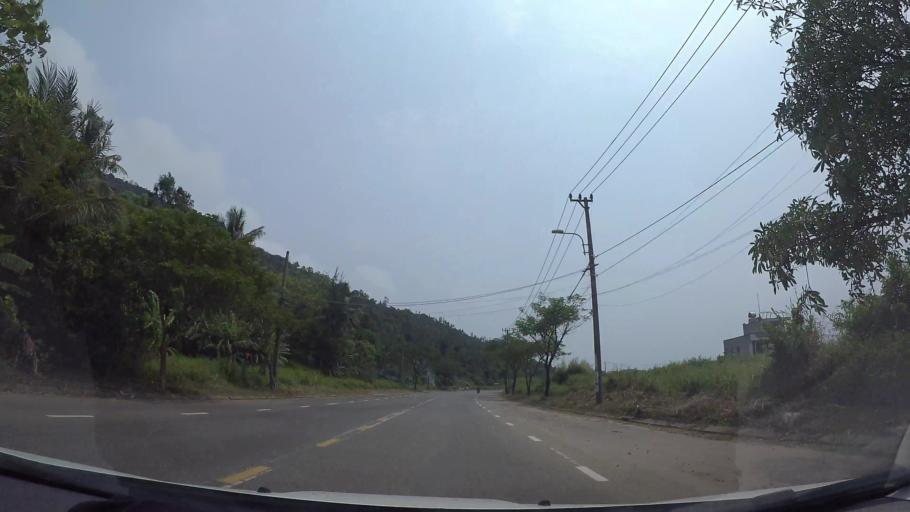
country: VN
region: Da Nang
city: Son Tra
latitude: 16.1075
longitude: 108.2626
